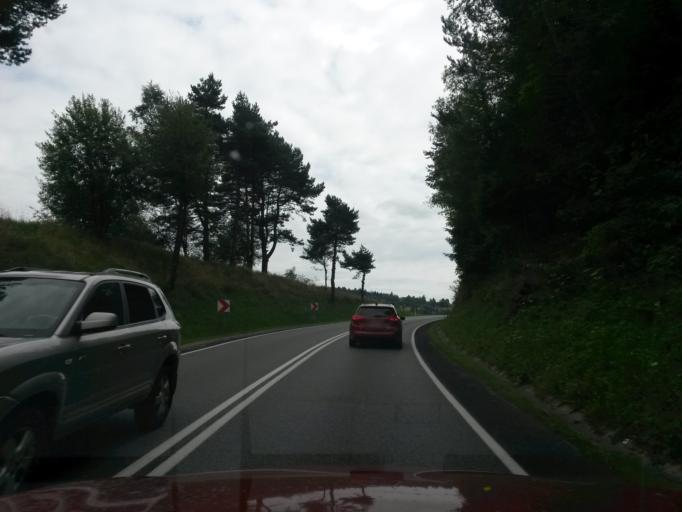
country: PL
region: Lesser Poland Voivodeship
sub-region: Powiat nowosadecki
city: Krynica-Zdroj
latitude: 49.4734
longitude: 20.9444
